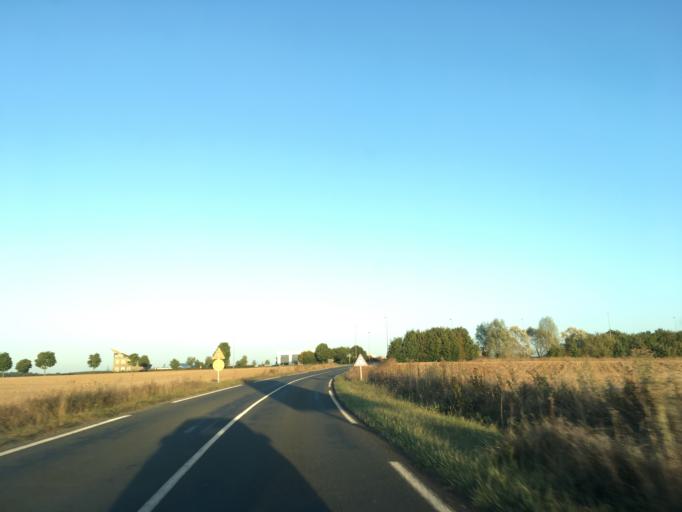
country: FR
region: Haute-Normandie
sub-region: Departement de l'Eure
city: Saint-Marcel
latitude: 49.0670
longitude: 1.4212
